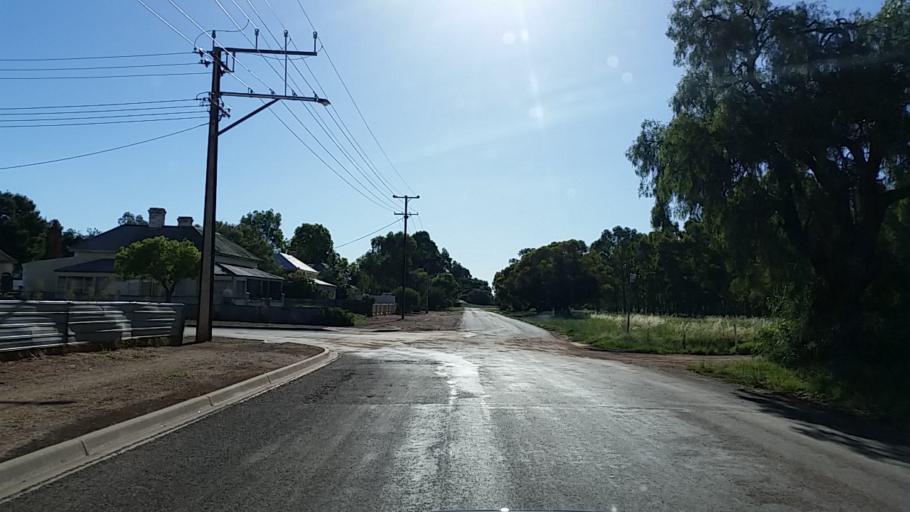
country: AU
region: South Australia
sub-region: Peterborough
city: Peterborough
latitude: -32.9729
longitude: 138.8306
